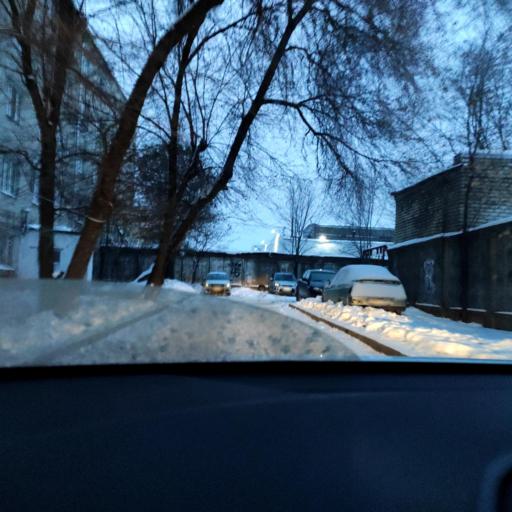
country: RU
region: Tatarstan
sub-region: Gorod Kazan'
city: Kazan
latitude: 55.8449
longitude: 49.0699
